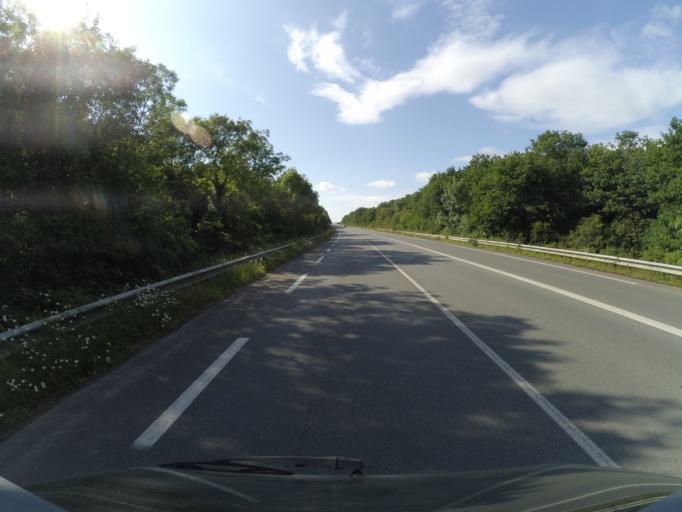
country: FR
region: Poitou-Charentes
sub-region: Departement de la Charente-Maritime
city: Saint-Agnant
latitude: 45.8356
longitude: -0.9408
